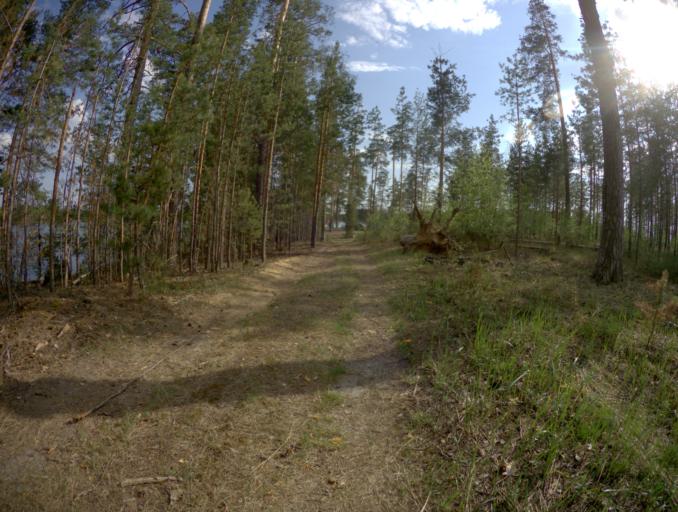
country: RU
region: Ivanovo
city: Talitsy
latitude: 56.4149
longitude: 42.2771
